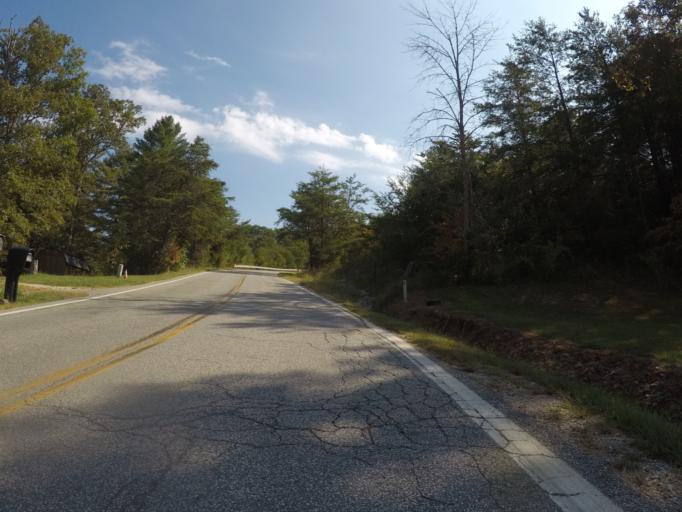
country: US
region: West Virginia
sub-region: Cabell County
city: Lesage
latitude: 38.5909
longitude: -82.4289
